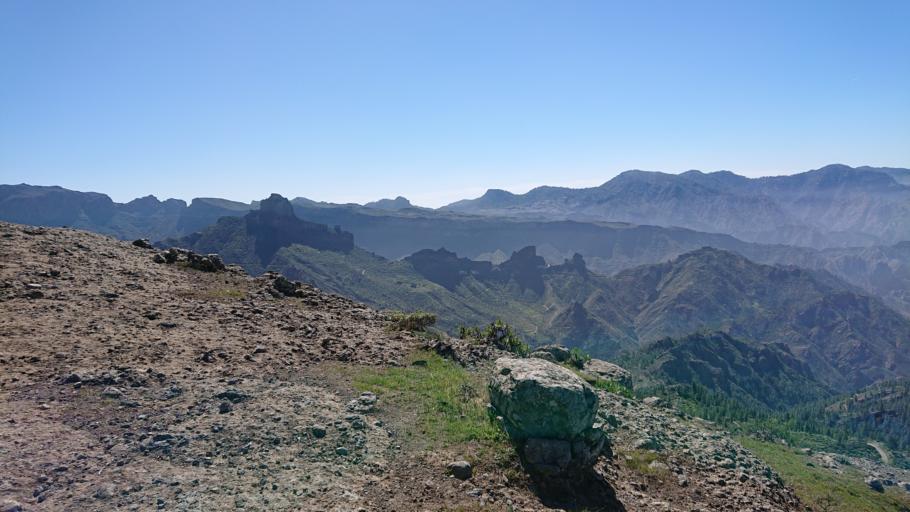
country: ES
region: Canary Islands
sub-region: Provincia de Las Palmas
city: Artenara
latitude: 28.0192
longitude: -15.6417
